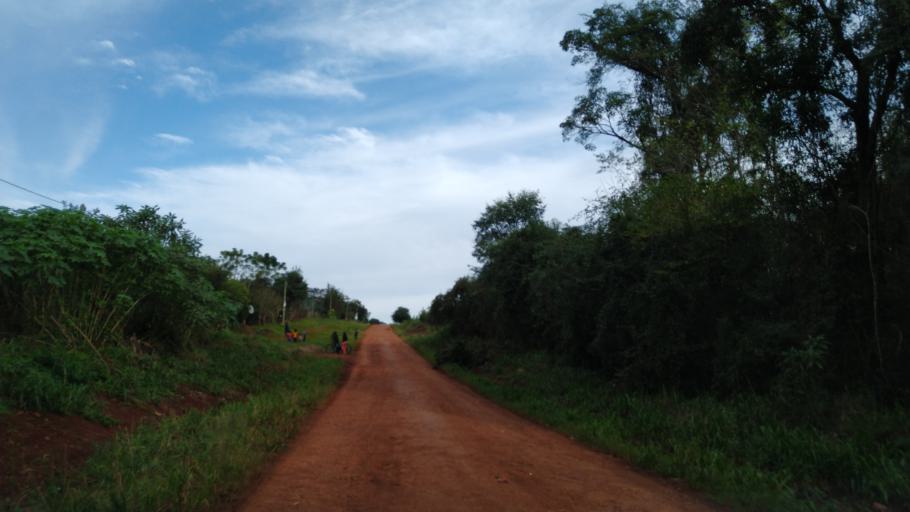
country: AR
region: Misiones
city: Capiovi
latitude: -26.9388
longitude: -55.0966
